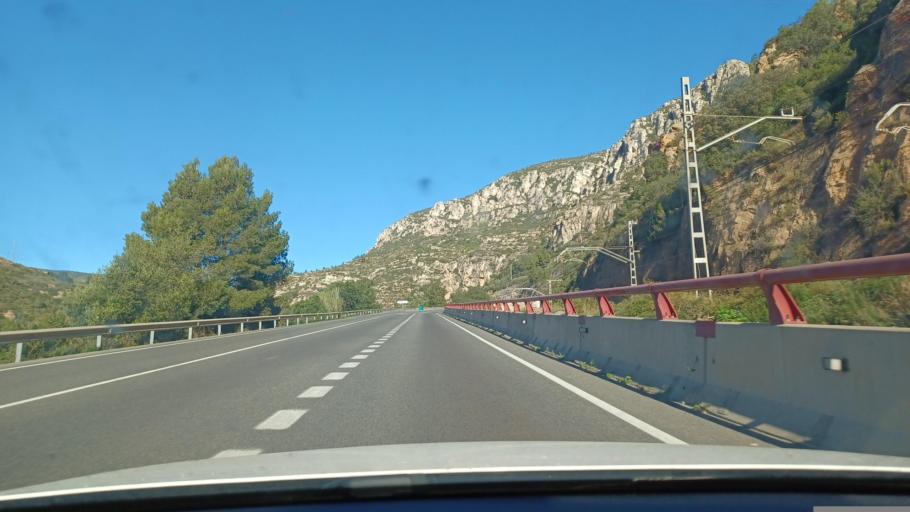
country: ES
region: Catalonia
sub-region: Provincia de Tarragona
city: Alcover
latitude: 41.3080
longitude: 1.1917
